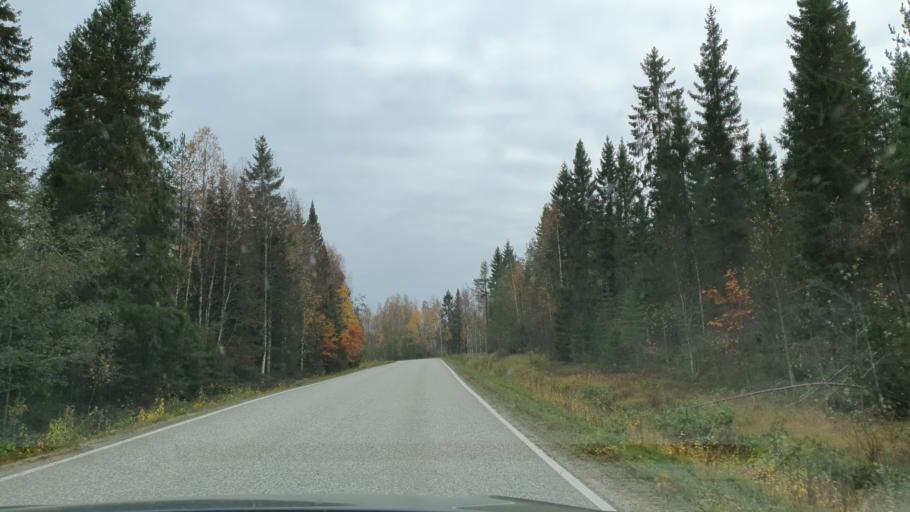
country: FI
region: Kainuu
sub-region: Kajaani
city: Ristijaervi
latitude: 64.4766
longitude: 28.2827
